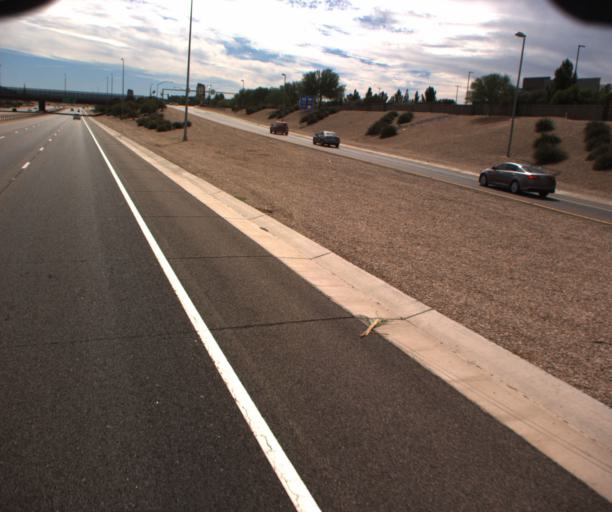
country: US
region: Arizona
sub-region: Maricopa County
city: Gilbert
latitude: 33.3097
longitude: -111.7396
